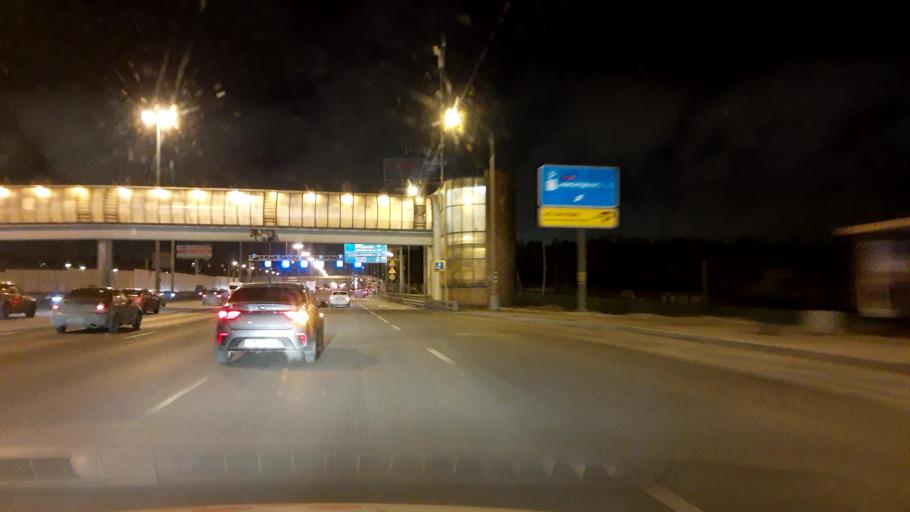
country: RU
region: Moscow
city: Solntsevo
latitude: 55.6180
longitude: 37.3865
